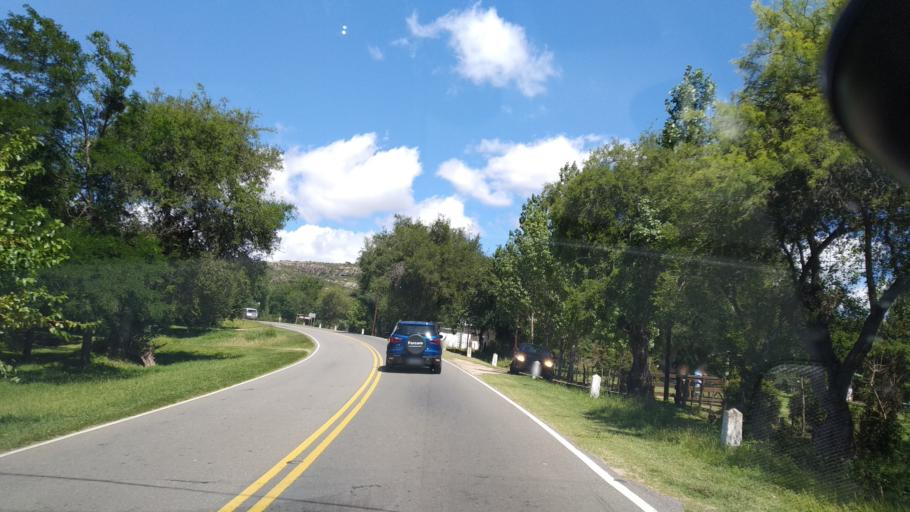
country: AR
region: Cordoba
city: Villa Cura Brochero
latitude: -31.6921
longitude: -65.0459
